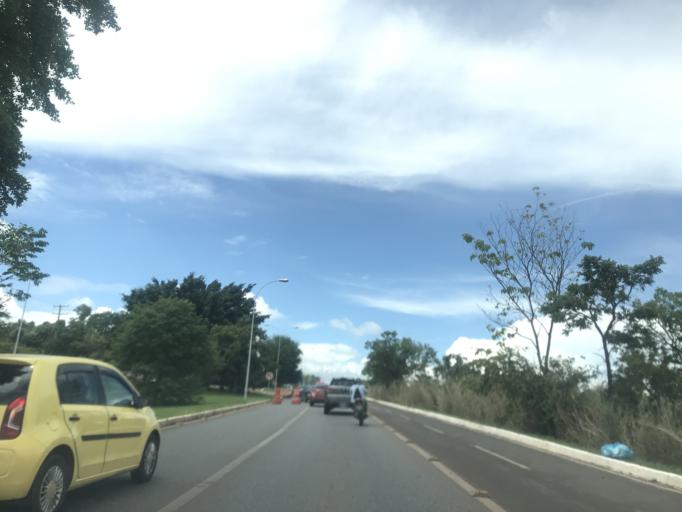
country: BR
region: Federal District
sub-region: Brasilia
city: Brasilia
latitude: -15.8067
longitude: -47.7986
